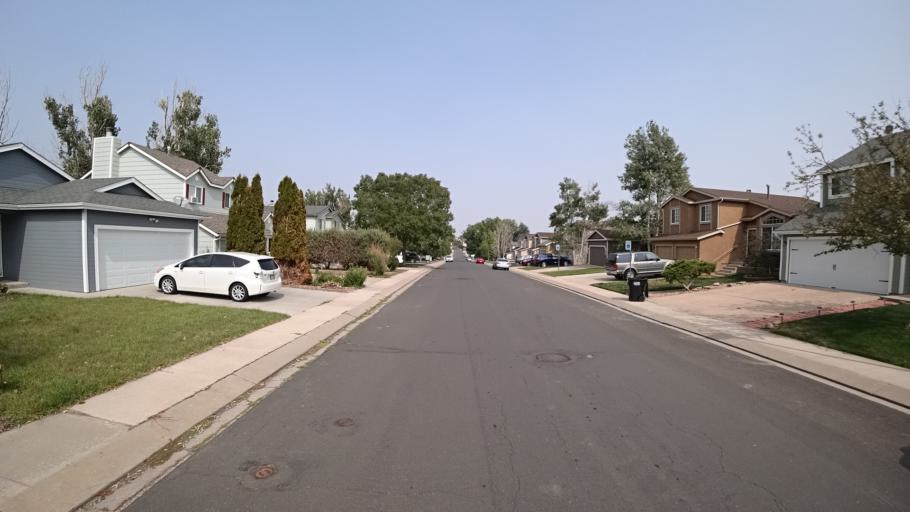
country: US
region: Colorado
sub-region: El Paso County
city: Cimarron Hills
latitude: 38.9178
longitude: -104.7274
